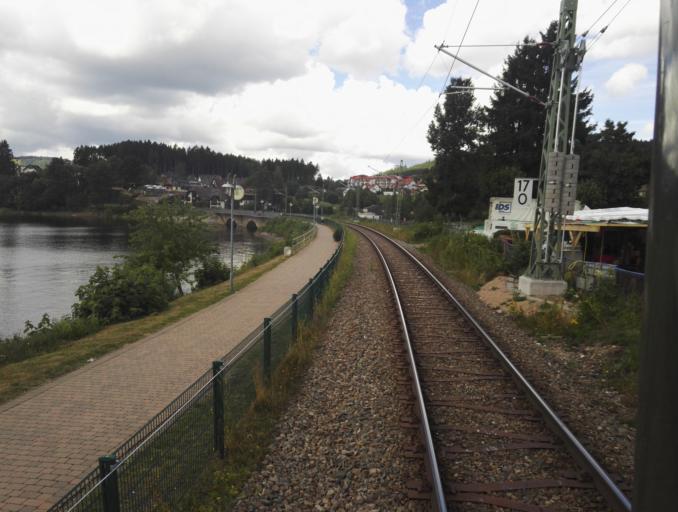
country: DE
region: Baden-Wuerttemberg
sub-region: Freiburg Region
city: Schluchsee
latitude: 47.8179
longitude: 8.1748
